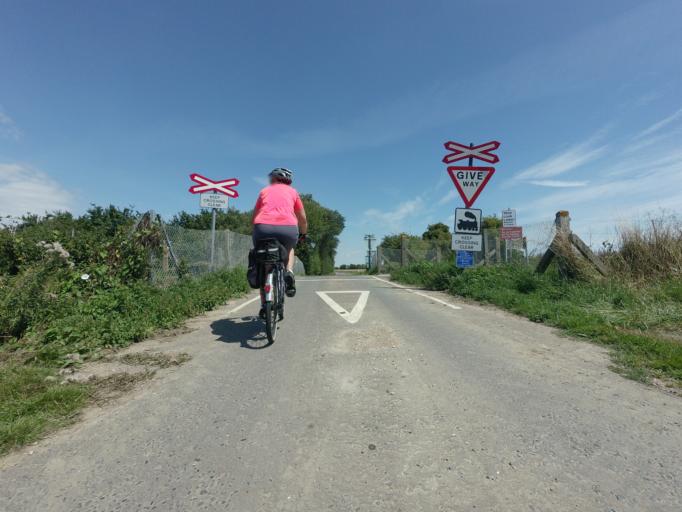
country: GB
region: England
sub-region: Kent
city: Lydd
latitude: 50.9840
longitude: 0.8689
